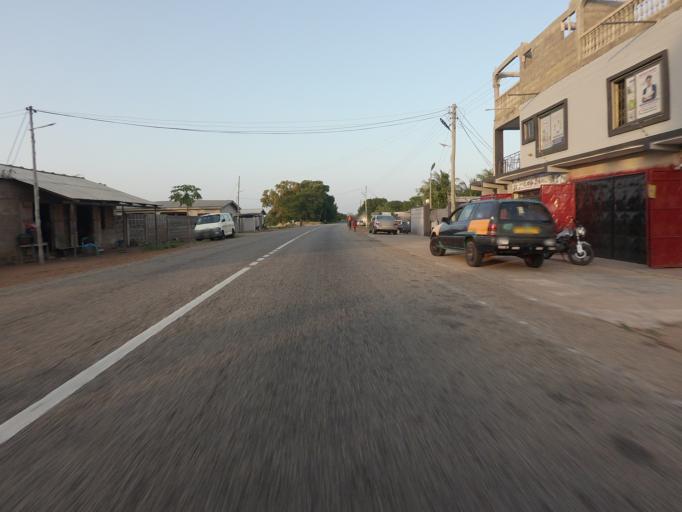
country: GH
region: Volta
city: Anloga
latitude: 5.7884
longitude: 0.8606
